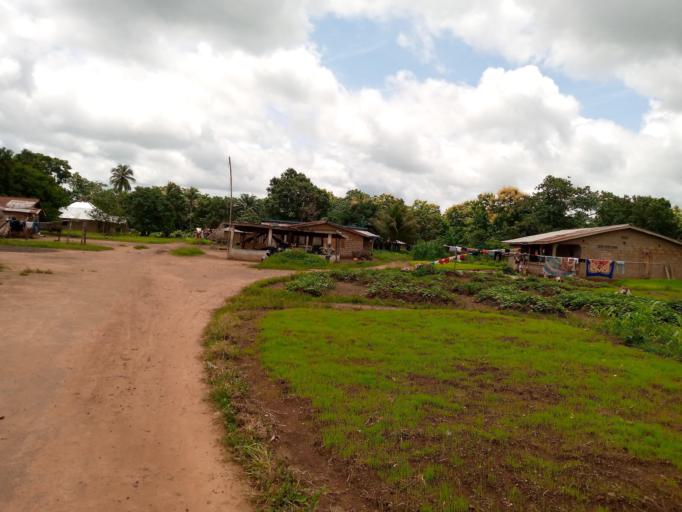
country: SL
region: Northern Province
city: Mange
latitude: 8.9918
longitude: -12.7809
